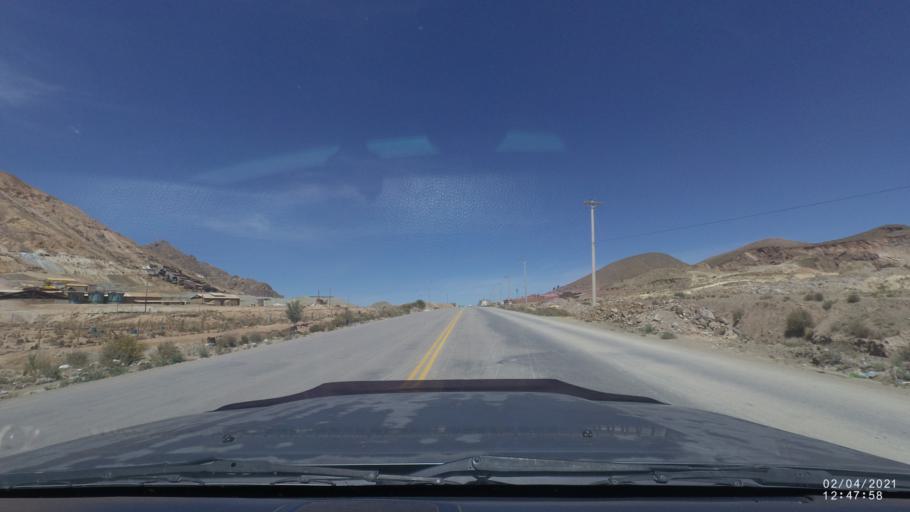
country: BO
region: Oruro
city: Oruro
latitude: -17.9591
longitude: -67.1427
